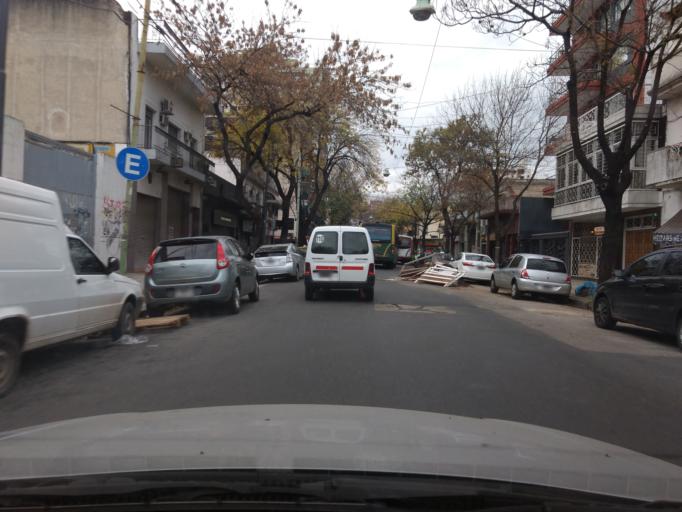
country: AR
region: Buenos Aires F.D.
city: Villa Santa Rita
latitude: -34.6192
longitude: -58.5010
